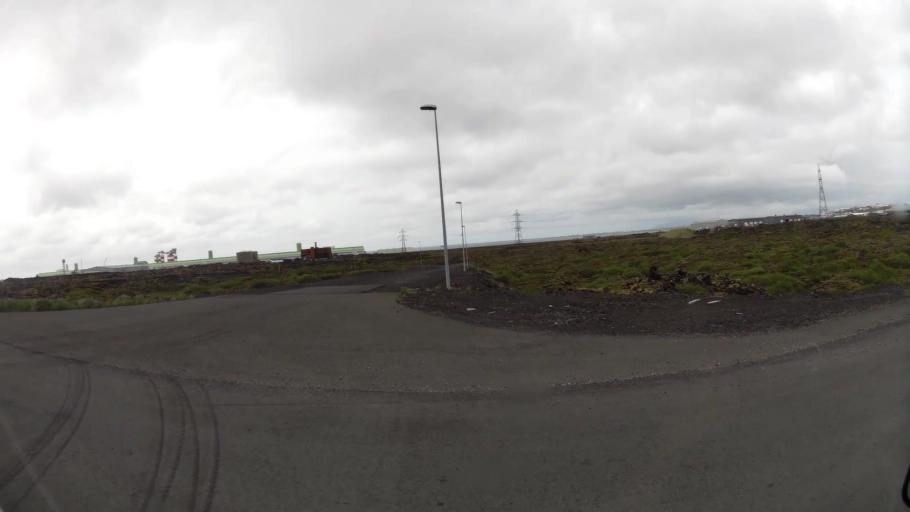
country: IS
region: Capital Region
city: Alftanes
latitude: 64.0408
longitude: -22.0087
